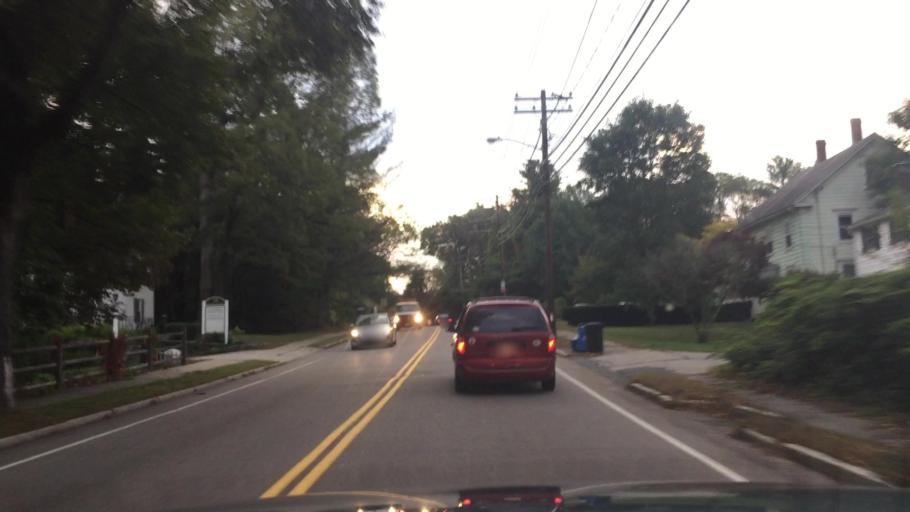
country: US
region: Massachusetts
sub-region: Norfolk County
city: Walpole
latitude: 42.1473
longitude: -71.2411
